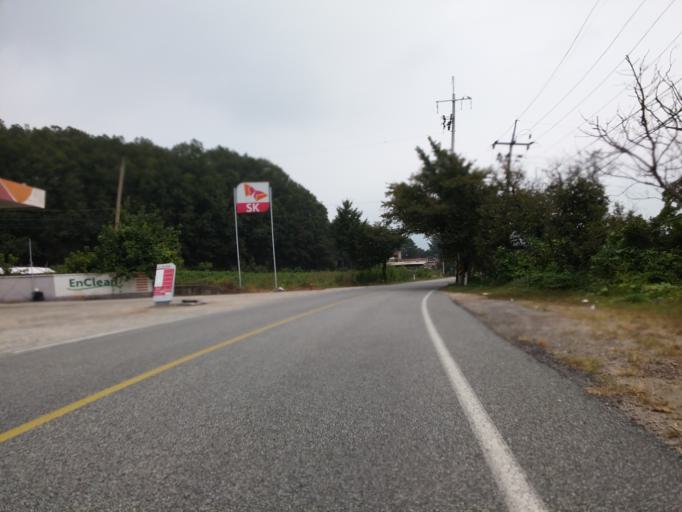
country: KR
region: Chungcheongbuk-do
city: Okcheon
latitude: 36.3928
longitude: 127.7129
